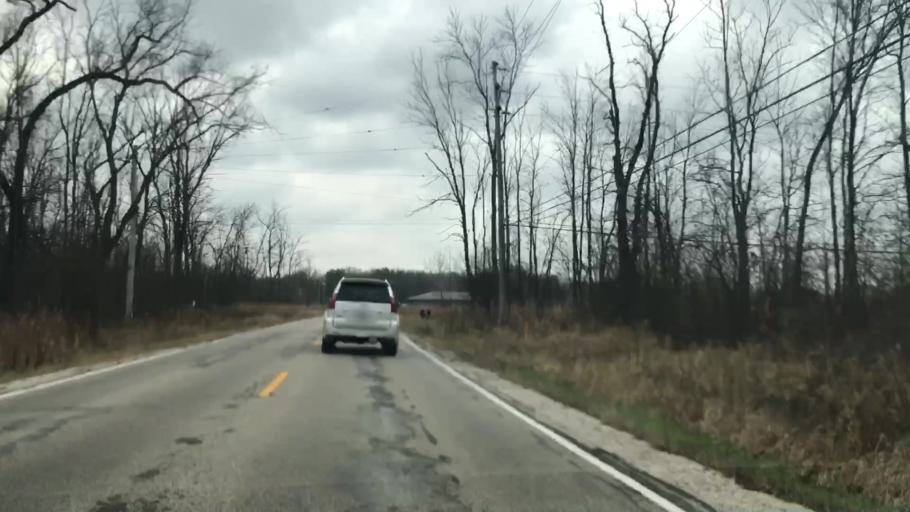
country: US
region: Wisconsin
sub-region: Waukesha County
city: Menomonee Falls
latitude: 43.1996
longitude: -88.1427
